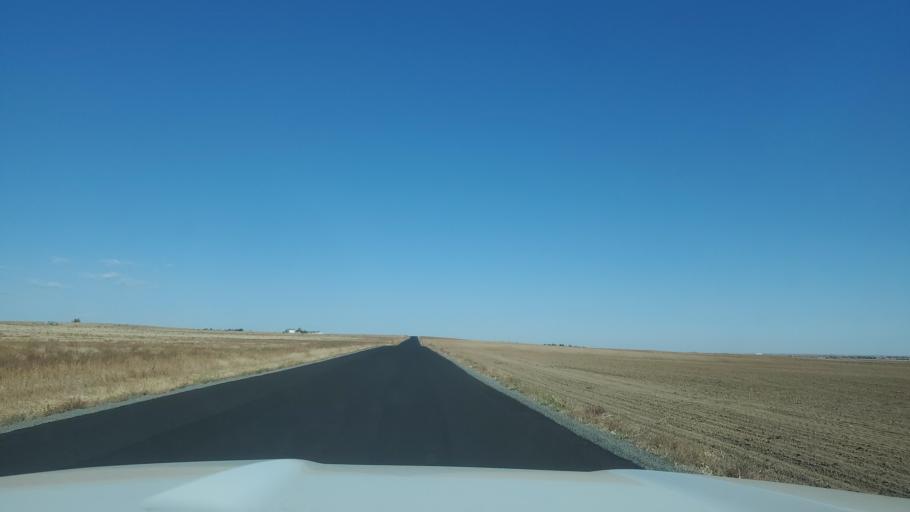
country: US
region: Colorado
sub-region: Adams County
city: Bennett
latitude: 39.7470
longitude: -104.3772
